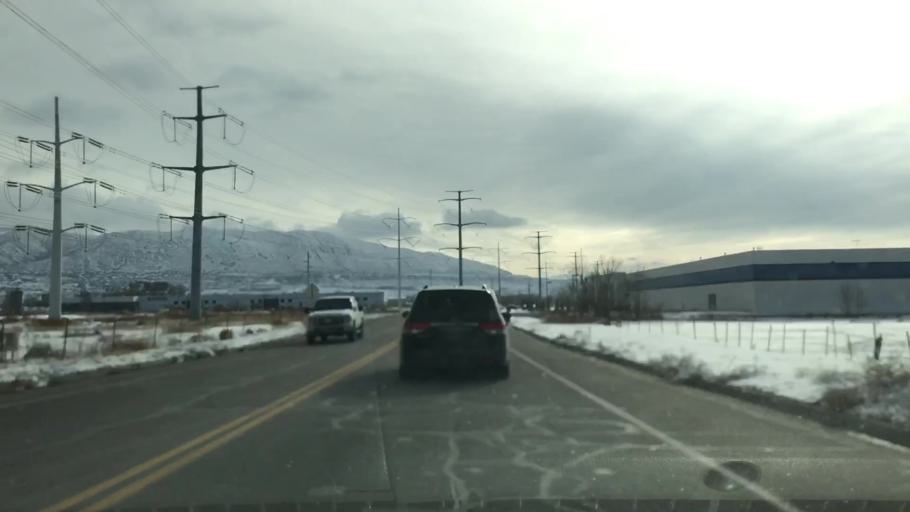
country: US
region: Utah
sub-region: Salt Lake County
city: Draper
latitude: 40.5249
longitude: -111.8942
